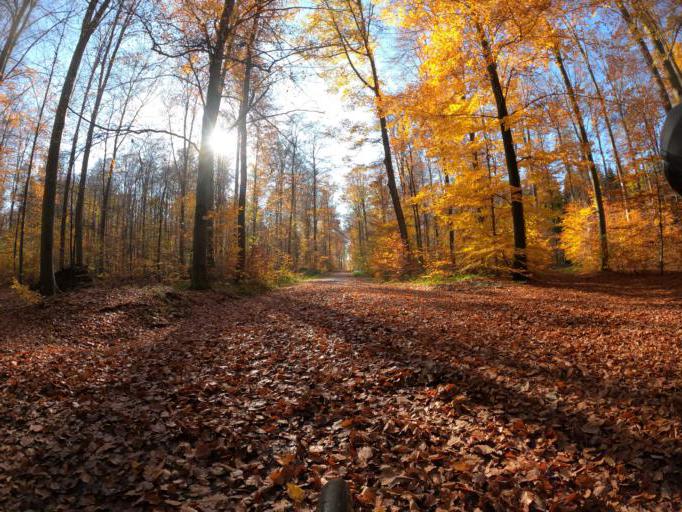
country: DE
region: Baden-Wuerttemberg
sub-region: Regierungsbezirk Stuttgart
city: Magstadt
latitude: 48.7545
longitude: 8.9836
